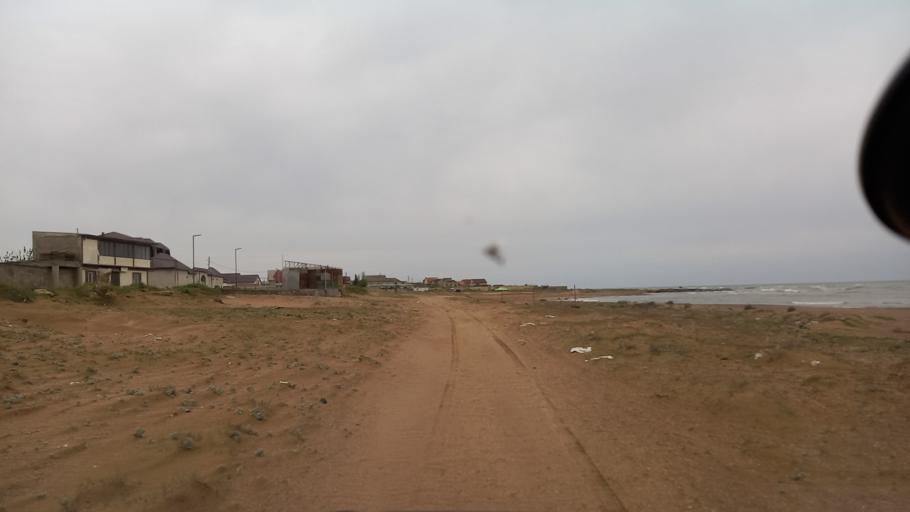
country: RU
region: Dagestan
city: Sabnova
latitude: 42.1192
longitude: 48.2664
